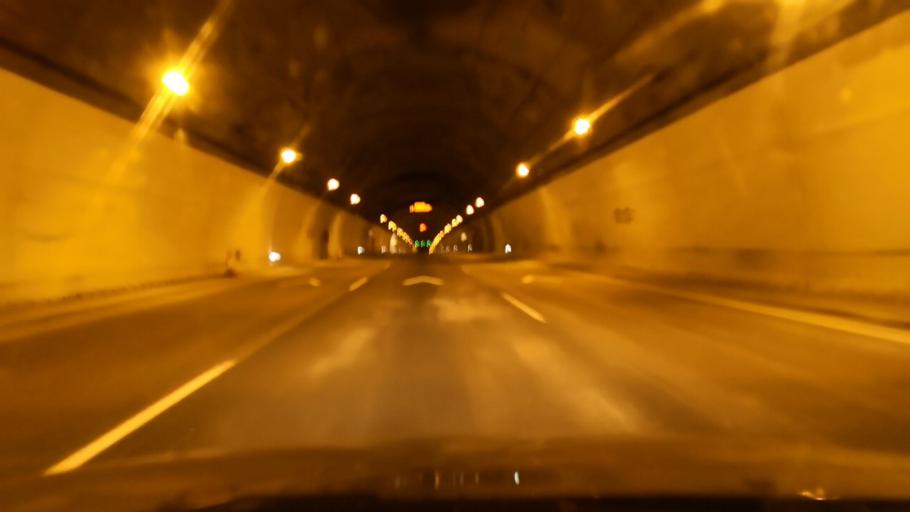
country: ES
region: Castille and Leon
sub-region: Provincia de Zamora
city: Requejo
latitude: 42.0376
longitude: -6.8166
